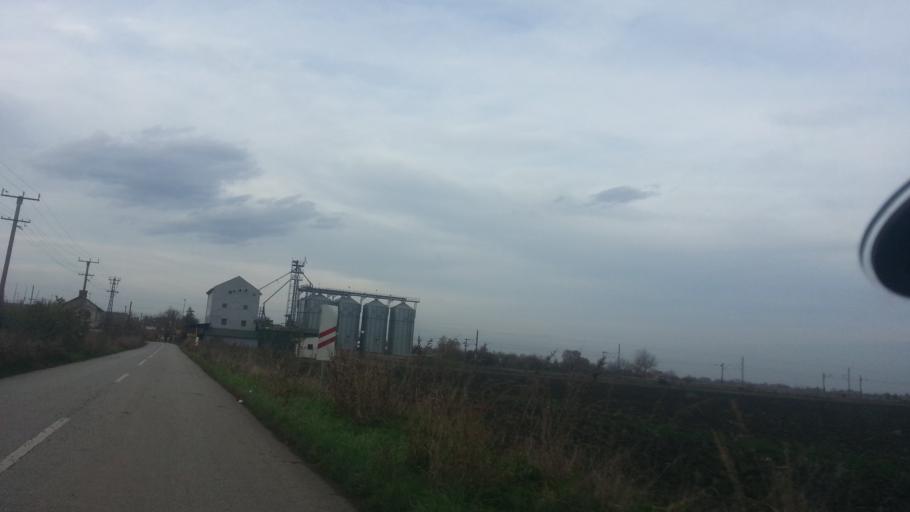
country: RS
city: Putinci
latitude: 44.9794
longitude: 19.9694
